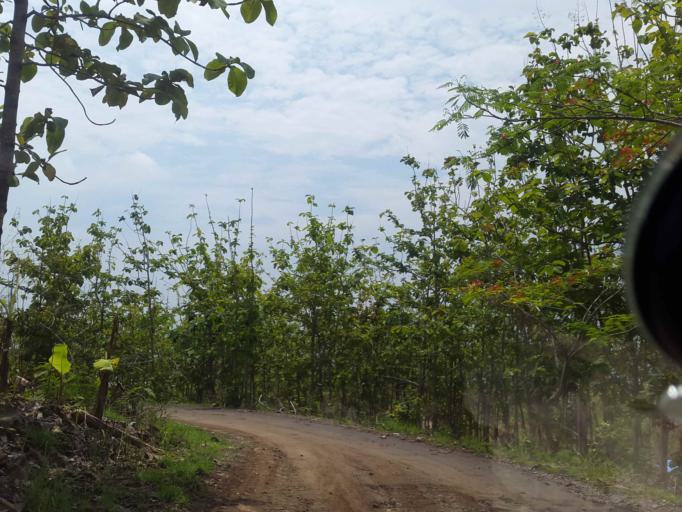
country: ID
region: East Java
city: Tumpakoyot
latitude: -8.3025
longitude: 112.0316
